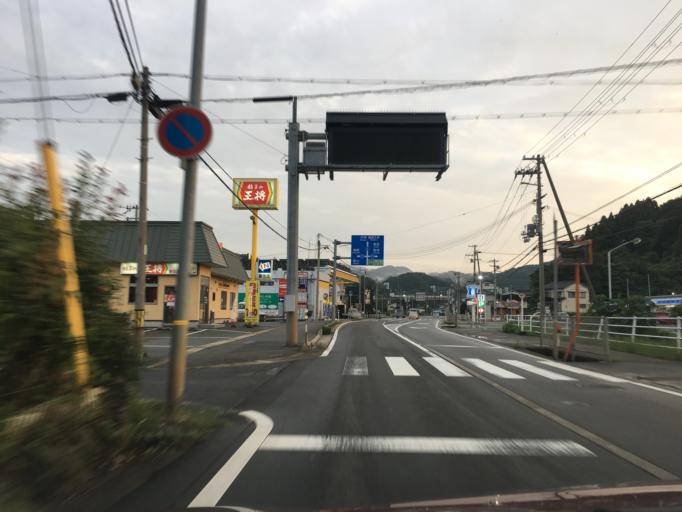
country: JP
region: Hyogo
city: Toyooka
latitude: 35.6327
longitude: 134.6268
